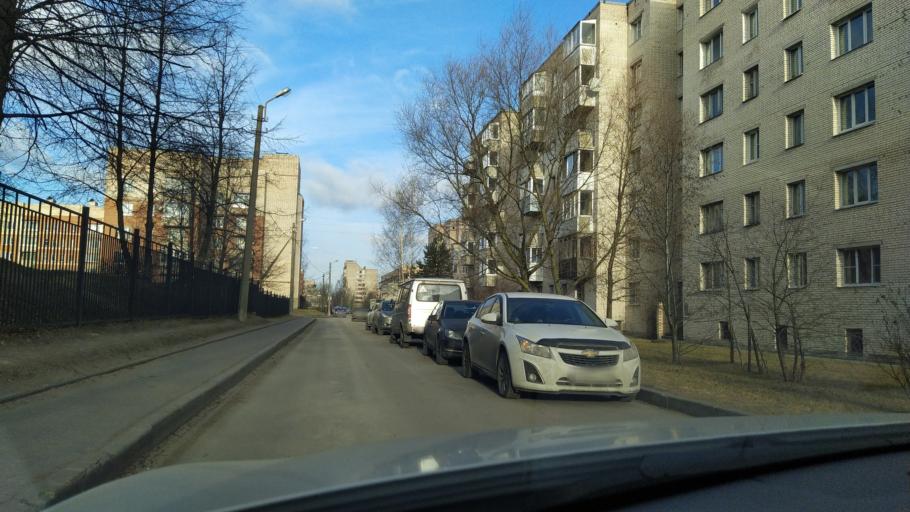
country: RU
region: St.-Petersburg
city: Pushkin
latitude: 59.7361
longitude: 30.4013
